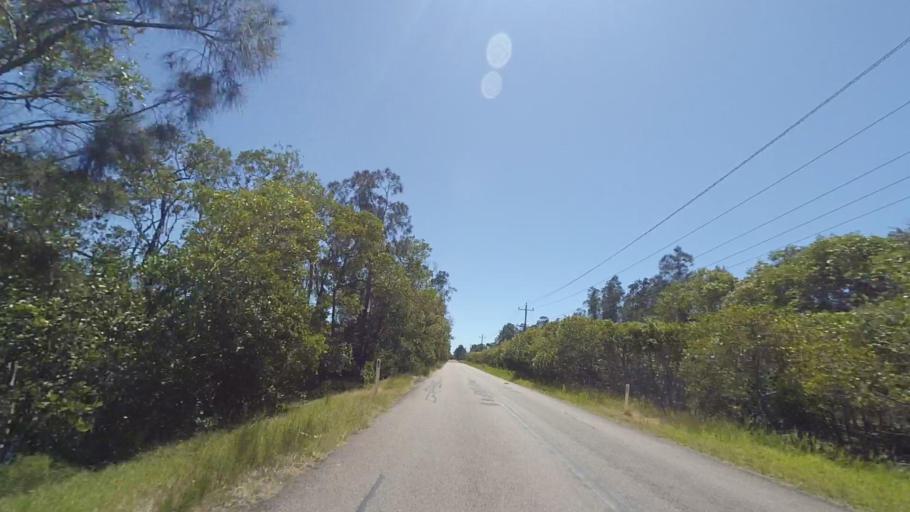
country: AU
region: New South Wales
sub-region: Port Stephens Shire
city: Medowie
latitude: -32.7853
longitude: 151.9382
